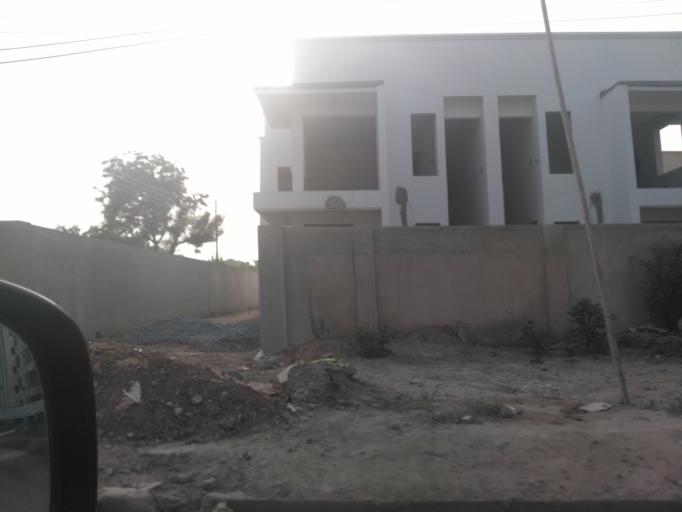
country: GH
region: Greater Accra
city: Accra
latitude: 5.6068
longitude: -0.2000
